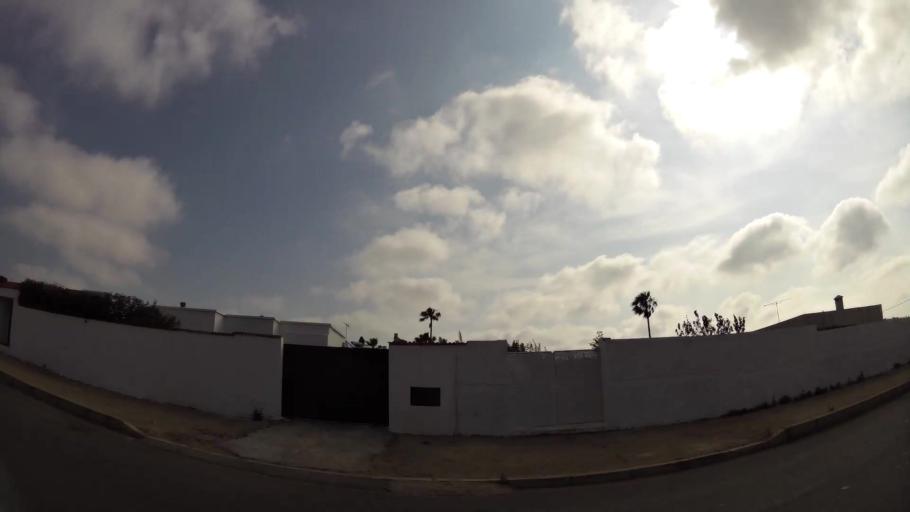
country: MA
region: Rabat-Sale-Zemmour-Zaer
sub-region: Rabat
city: Rabat
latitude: 33.9691
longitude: -6.8491
